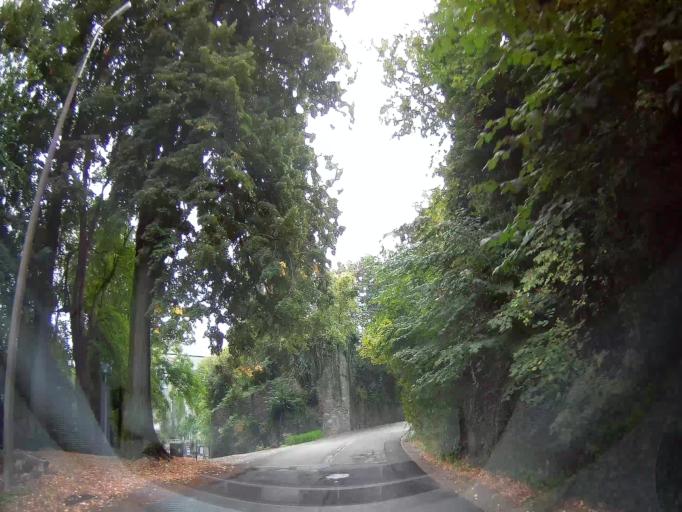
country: BE
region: Wallonia
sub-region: Province de Liege
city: Limbourg
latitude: 50.6141
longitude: 5.9412
